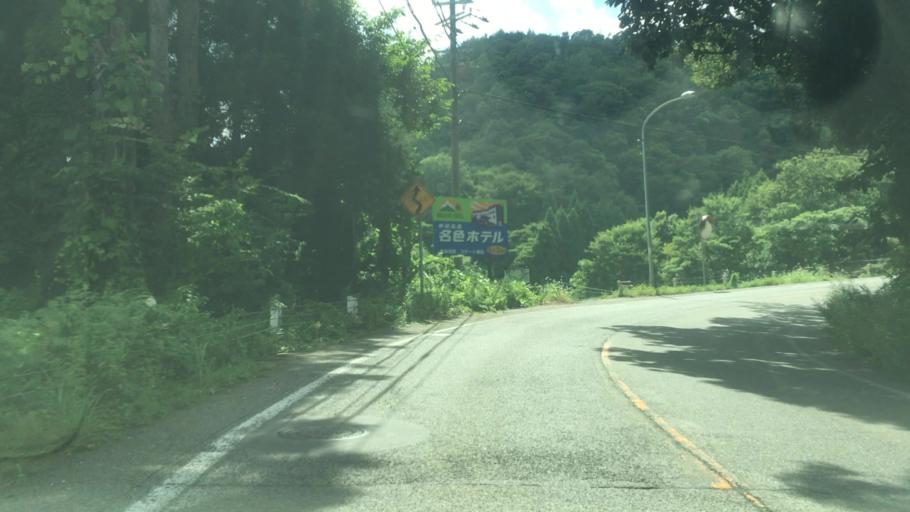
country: JP
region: Hyogo
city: Toyooka
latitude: 35.4886
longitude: 134.6897
